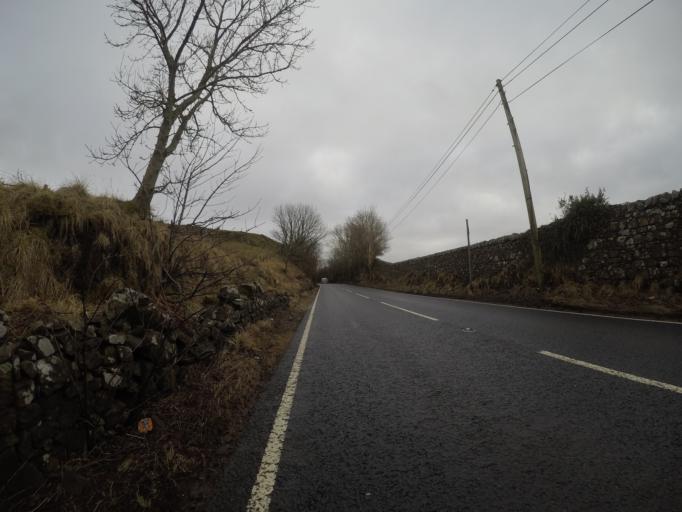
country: GB
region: Scotland
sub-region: North Ayrshire
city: Fairlie
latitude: 55.7776
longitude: -4.8417
